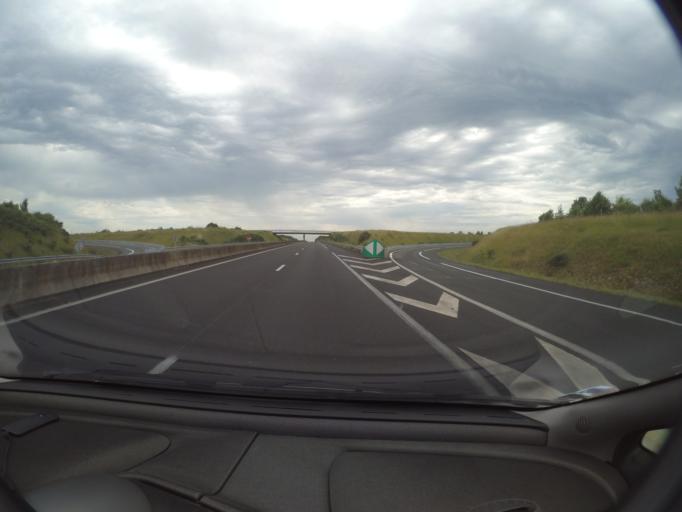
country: FR
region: Pays de la Loire
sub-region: Departement de Maine-et-Loire
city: Saint-Lambert-la-Potherie
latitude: 47.4669
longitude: -0.6884
